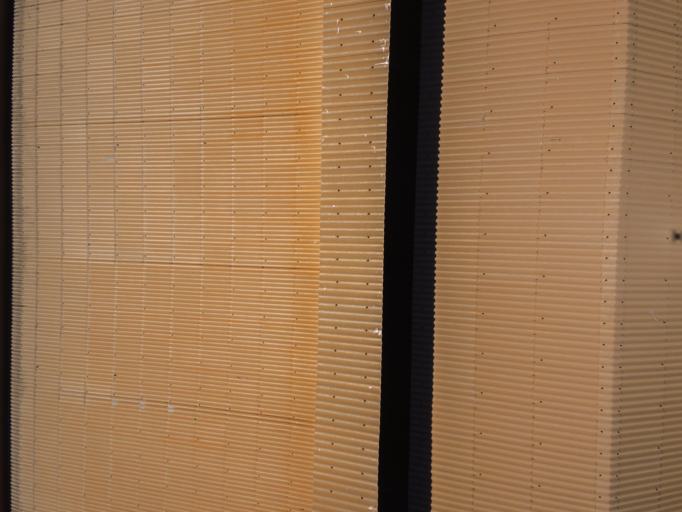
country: BR
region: Sao Paulo
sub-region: Jacarei
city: Jacarei
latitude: -23.2898
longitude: -45.9343
